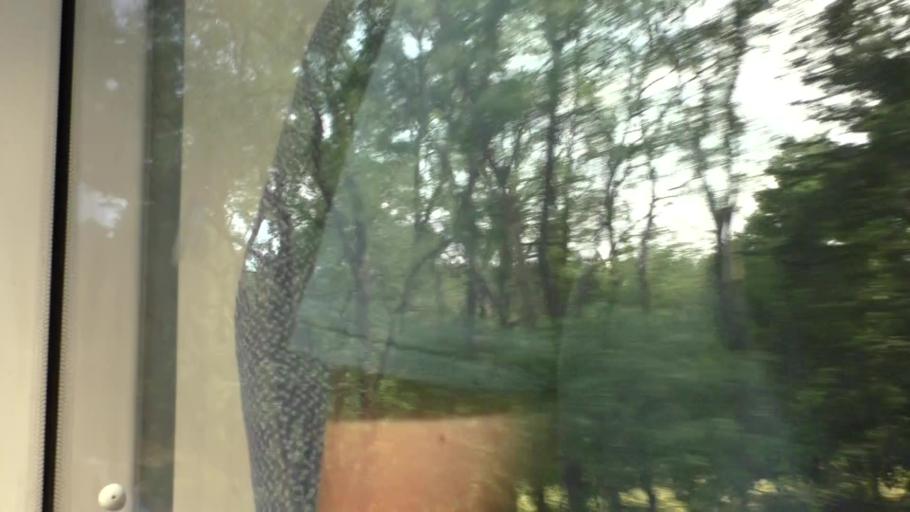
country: DE
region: Brandenburg
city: Diensdorf-Radlow
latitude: 52.2018
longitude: 14.0905
